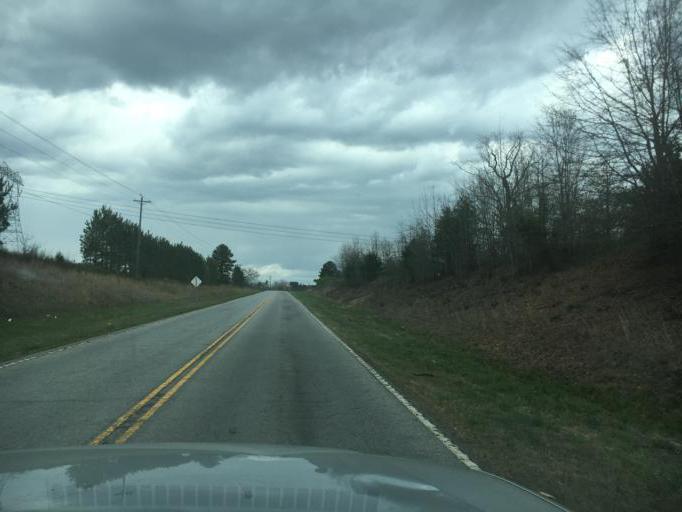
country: US
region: South Carolina
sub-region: Oconee County
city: Walhalla
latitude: 34.7210
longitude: -83.0549
